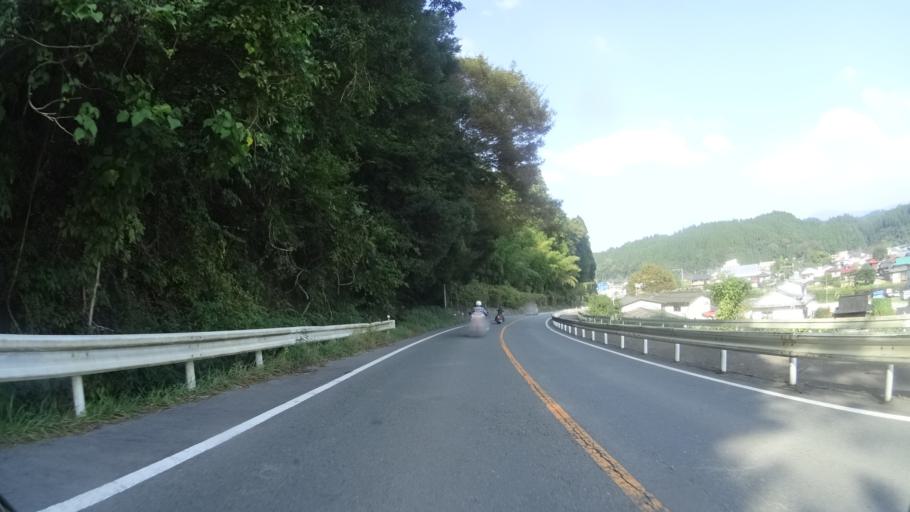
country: JP
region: Kumamoto
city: Aso
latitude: 33.0949
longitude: 131.0664
